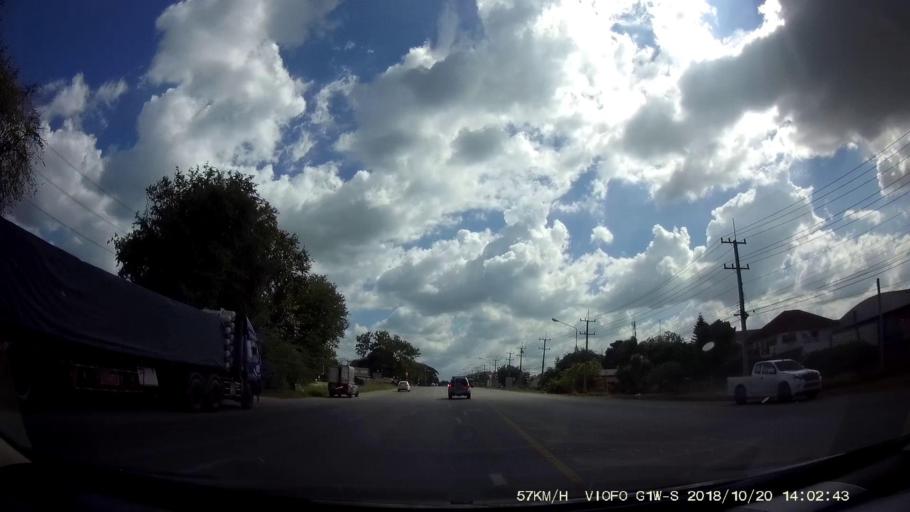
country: TH
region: Khon Kaen
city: Chum Phae
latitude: 16.4890
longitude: 102.1247
